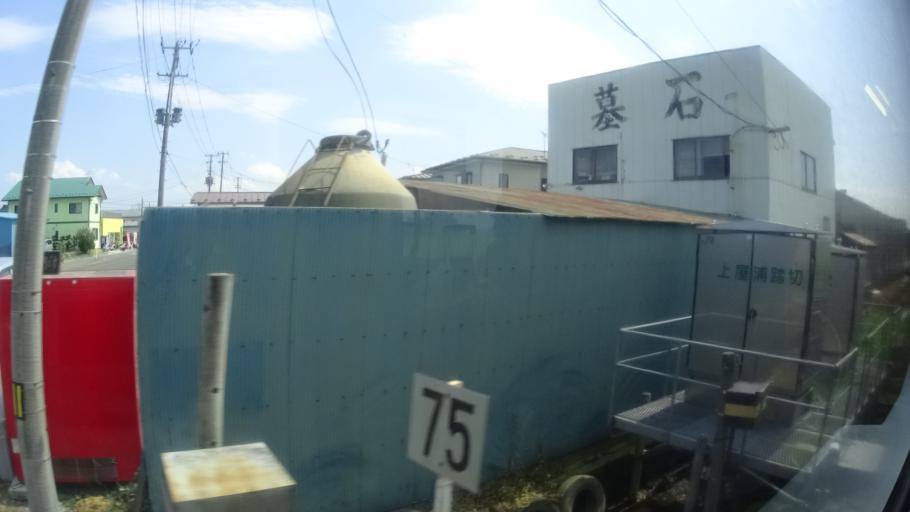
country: JP
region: Miyagi
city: Wakuya
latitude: 38.5813
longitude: 141.2410
